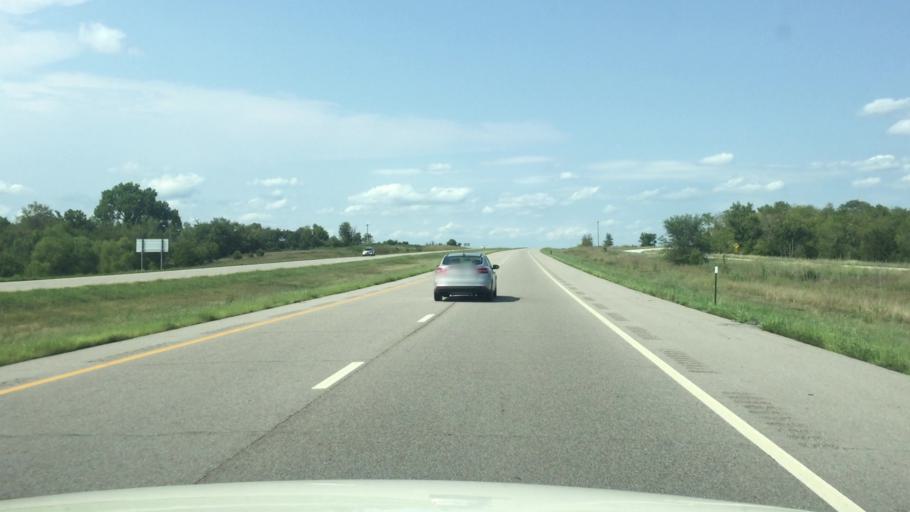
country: US
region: Kansas
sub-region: Linn County
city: La Cygne
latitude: 38.4147
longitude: -94.6875
